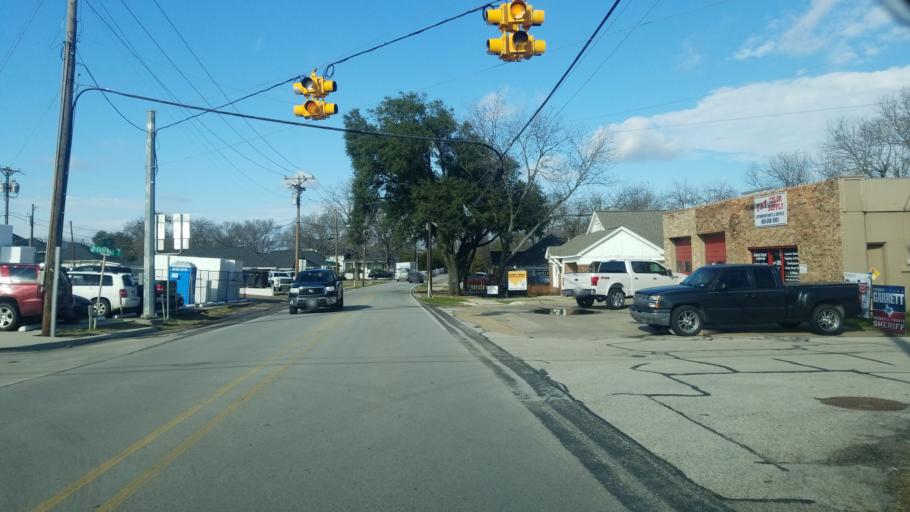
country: US
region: Texas
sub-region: Rockwall County
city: Rockwall
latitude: 32.9316
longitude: -96.4586
